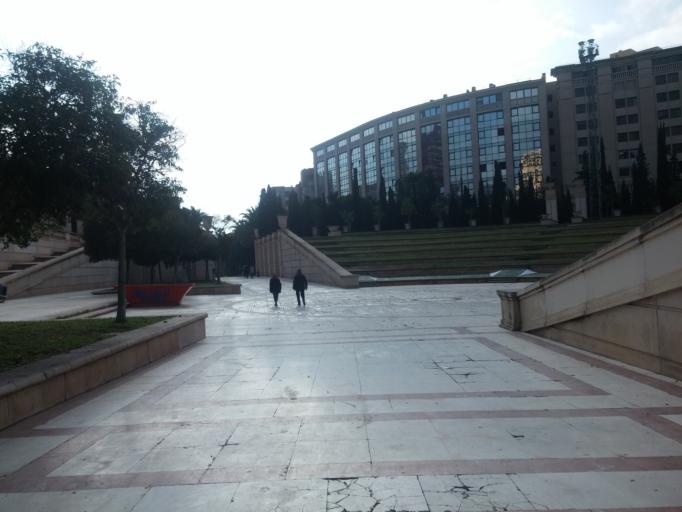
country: ES
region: Valencia
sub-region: Provincia de Alicante
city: Benidorm
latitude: 38.5425
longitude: -0.1305
